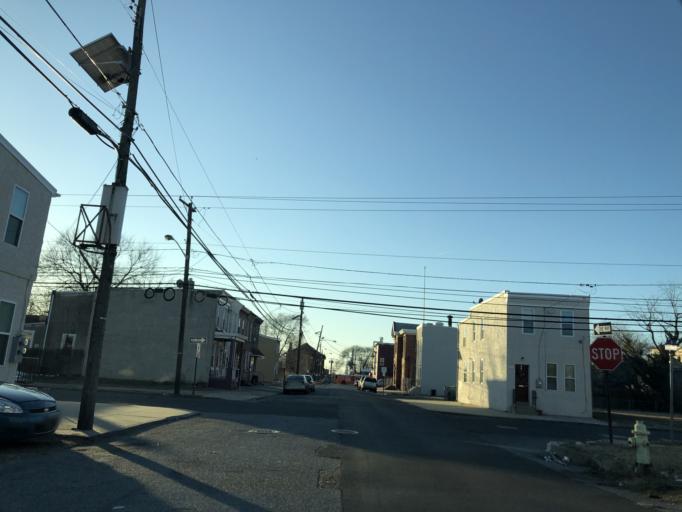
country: US
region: New Jersey
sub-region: Camden County
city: Camden
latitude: 39.9332
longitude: -75.1174
